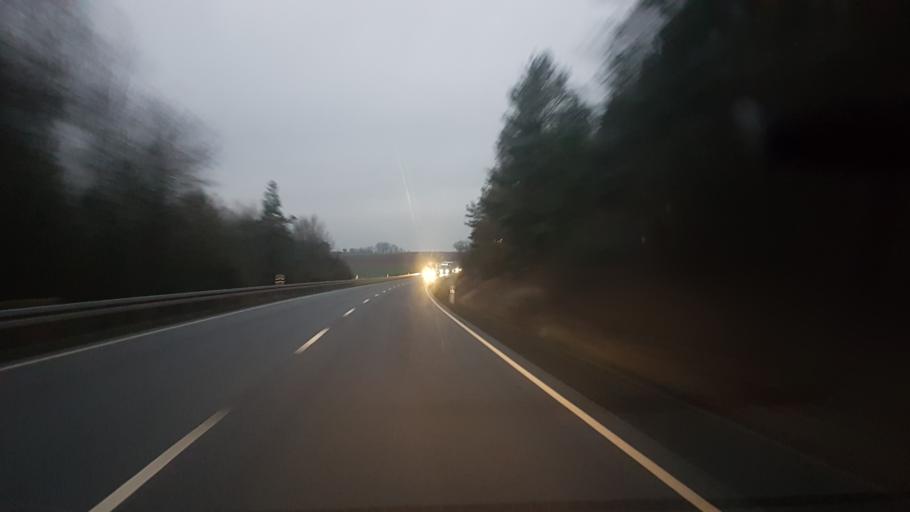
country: DE
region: Bavaria
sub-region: Regierungsbezirk Unterfranken
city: Bundorf
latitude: 50.2549
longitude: 10.5507
